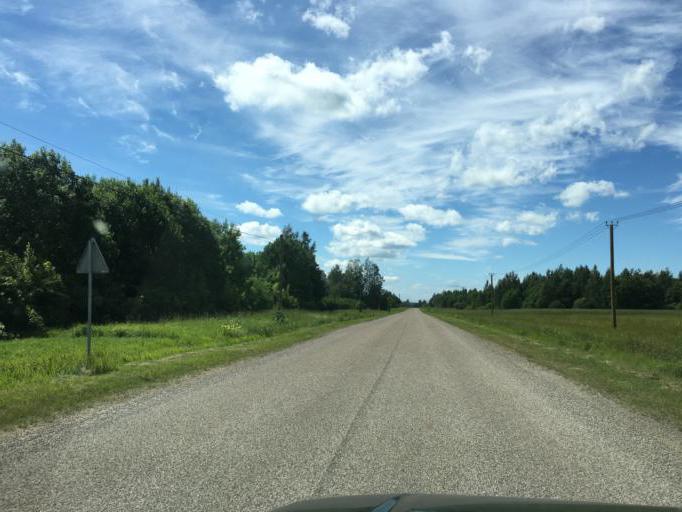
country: LV
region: Balvu Rajons
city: Balvi
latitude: 57.1446
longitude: 27.2960
